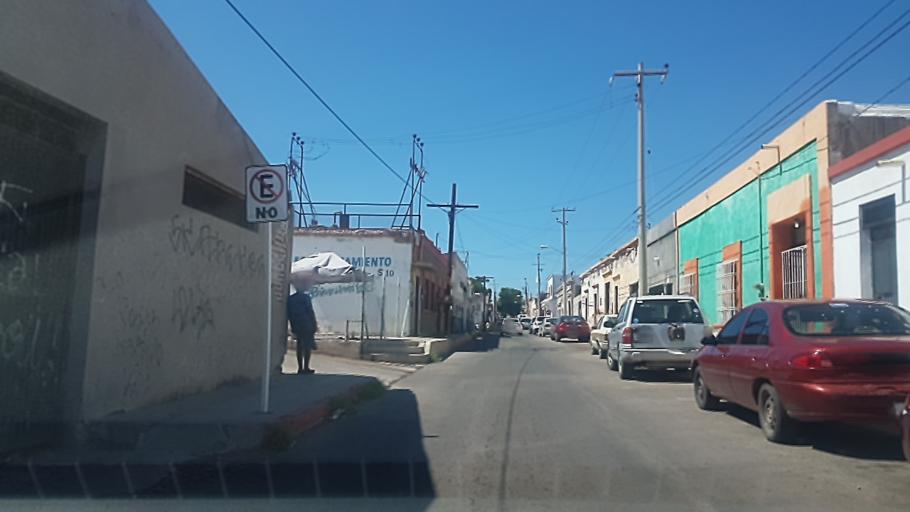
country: MX
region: Sonora
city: Heroica Guaymas
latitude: 27.9241
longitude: -110.8951
